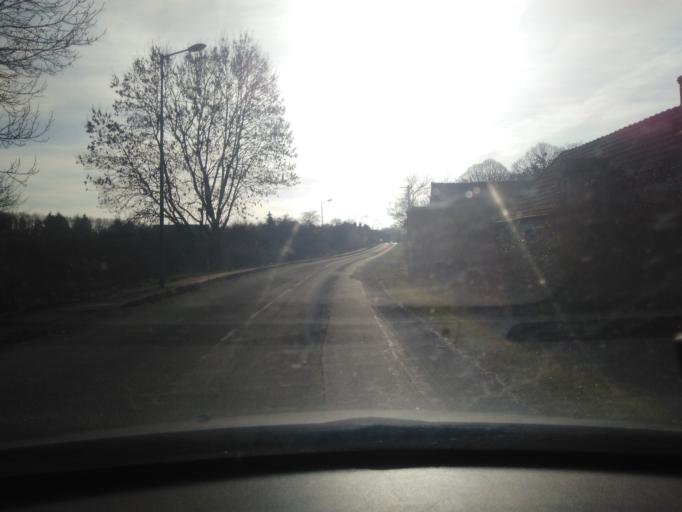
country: FR
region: Bourgogne
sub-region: Departement de la Nievre
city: Saint-Parize-le-Chatel
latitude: 46.8230
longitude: 3.2470
